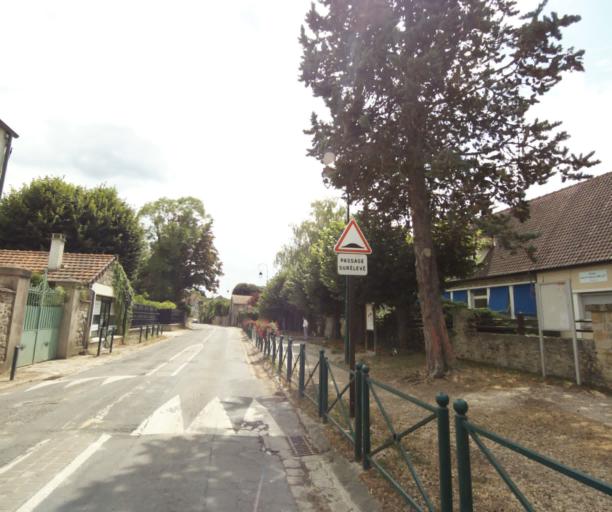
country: FR
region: Ile-de-France
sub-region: Departement de Seine-et-Marne
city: Barbizon
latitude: 48.4479
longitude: 2.6022
